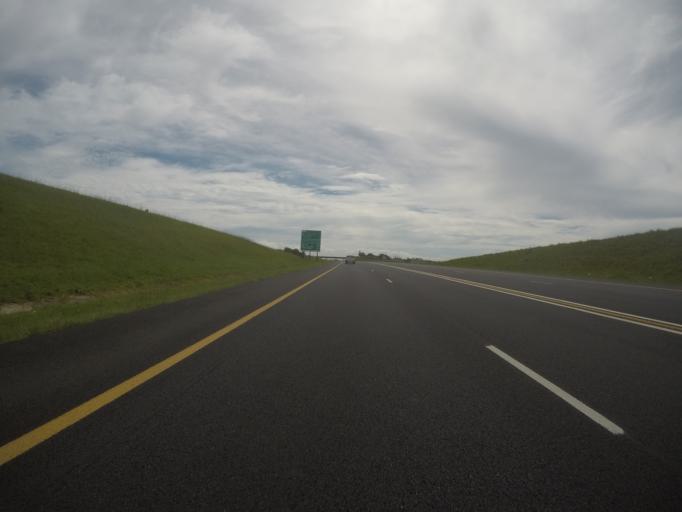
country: ZA
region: KwaZulu-Natal
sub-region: iLembe District Municipality
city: Mandeni
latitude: -29.0883
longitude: 31.6068
